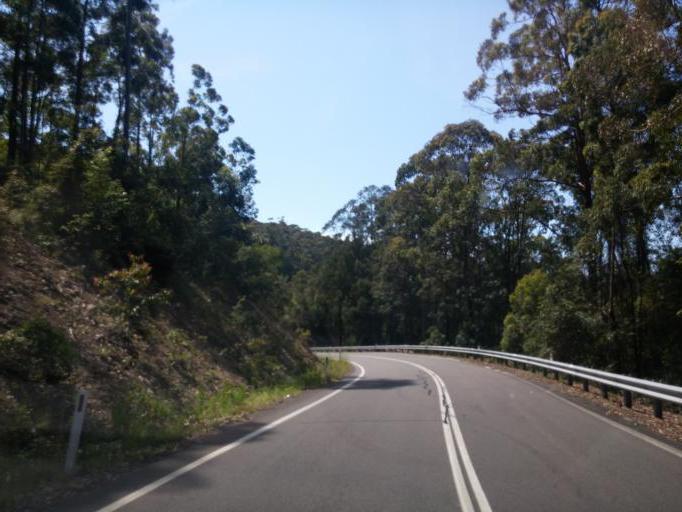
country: AU
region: New South Wales
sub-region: Great Lakes
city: Bulahdelah
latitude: -32.3890
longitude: 152.2477
